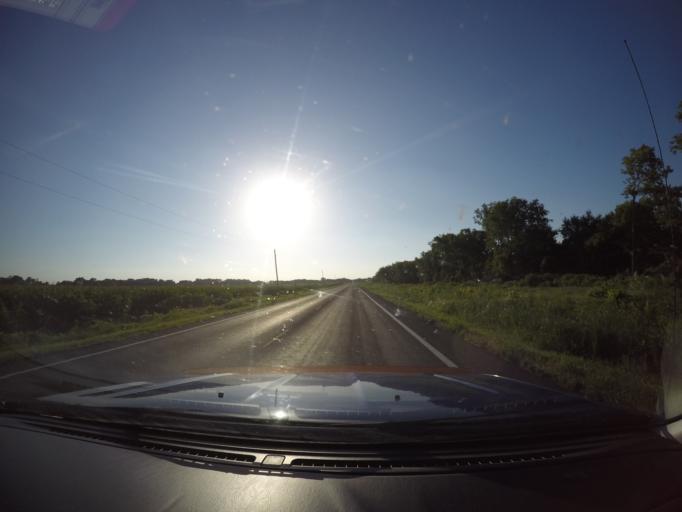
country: US
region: Kansas
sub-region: Pottawatomie County
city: Saint Marys
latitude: 39.2077
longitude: -96.1029
